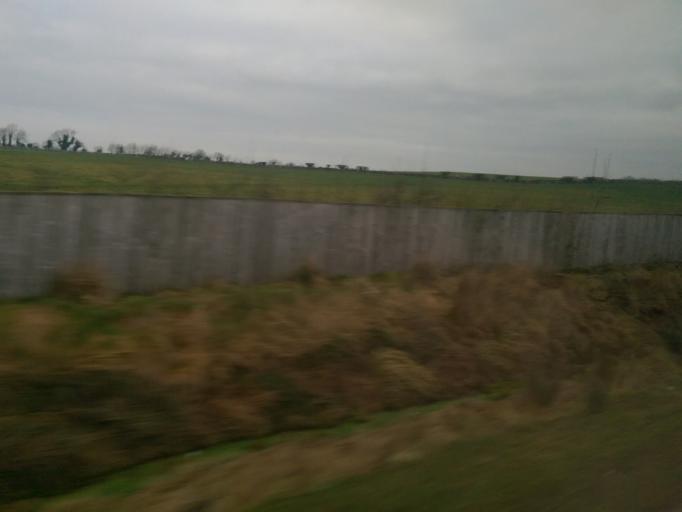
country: IE
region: Connaught
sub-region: County Galway
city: Ballinasloe
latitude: 53.3207
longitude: -8.1512
